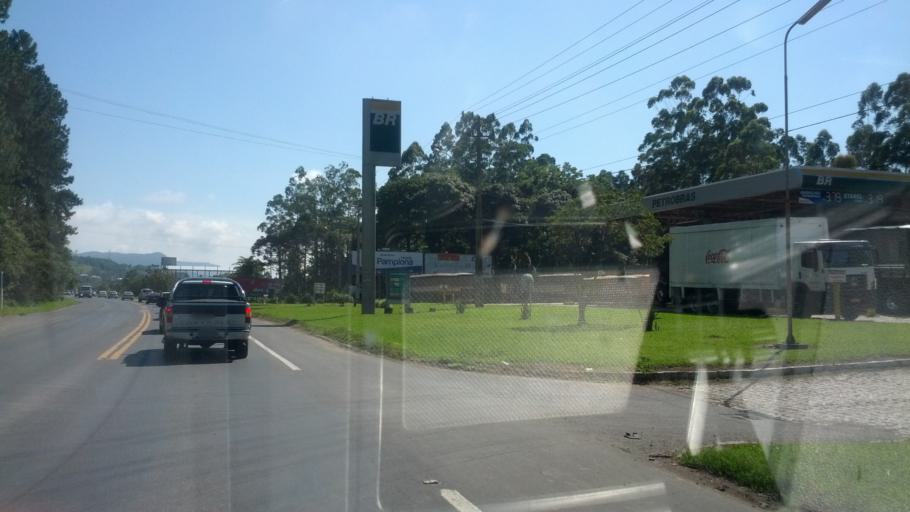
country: BR
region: Santa Catarina
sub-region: Rio Do Sul
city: Rio do Sul
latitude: -27.2323
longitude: -49.6716
